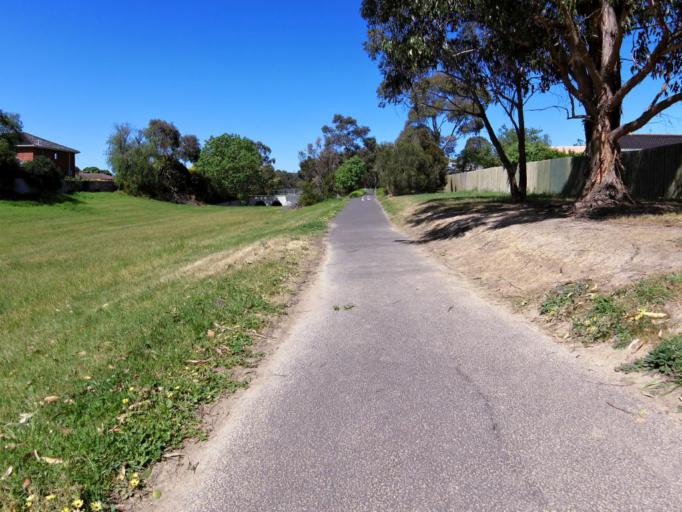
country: AU
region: Victoria
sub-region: Knox
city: Rowville
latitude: -37.9305
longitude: 145.2391
